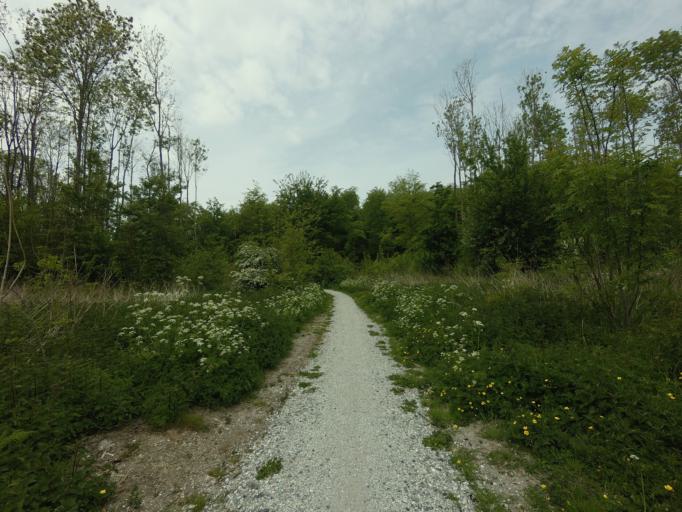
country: NL
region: Friesland
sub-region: Sudwest Fryslan
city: Bolsward
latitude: 53.0954
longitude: 5.4764
